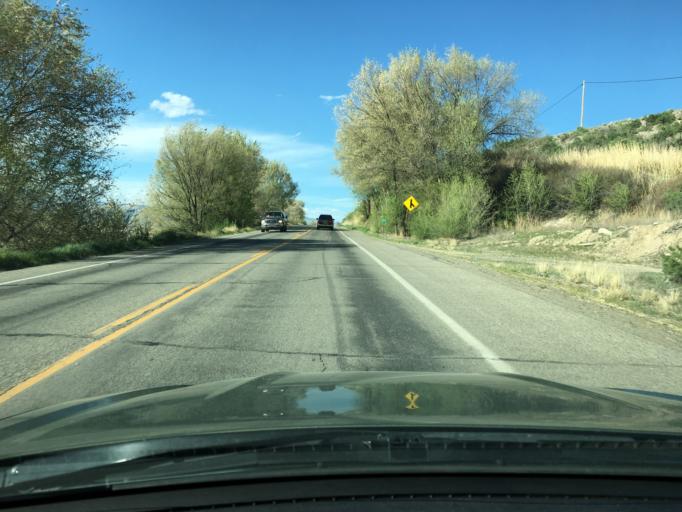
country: US
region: Colorado
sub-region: Delta County
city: Orchard City
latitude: 38.7748
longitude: -108.0012
